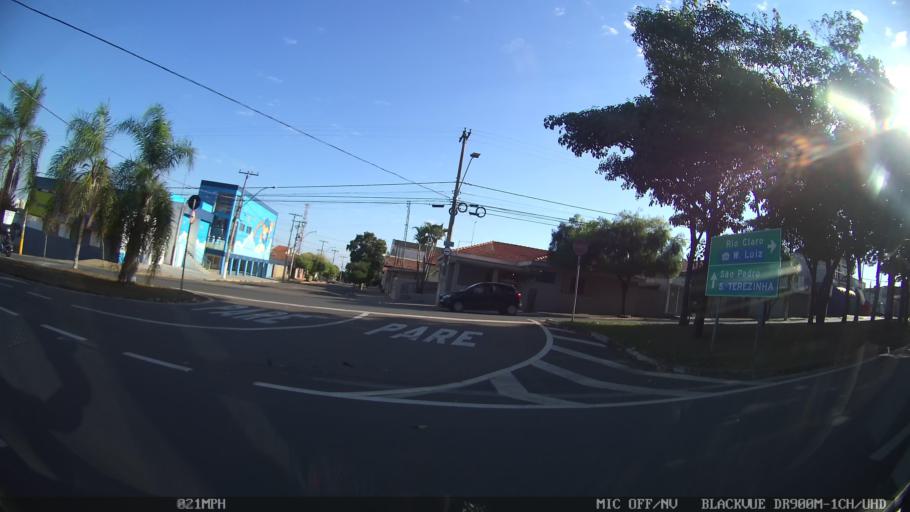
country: BR
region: Sao Paulo
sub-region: Piracicaba
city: Piracicaba
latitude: -22.6999
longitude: -47.6526
